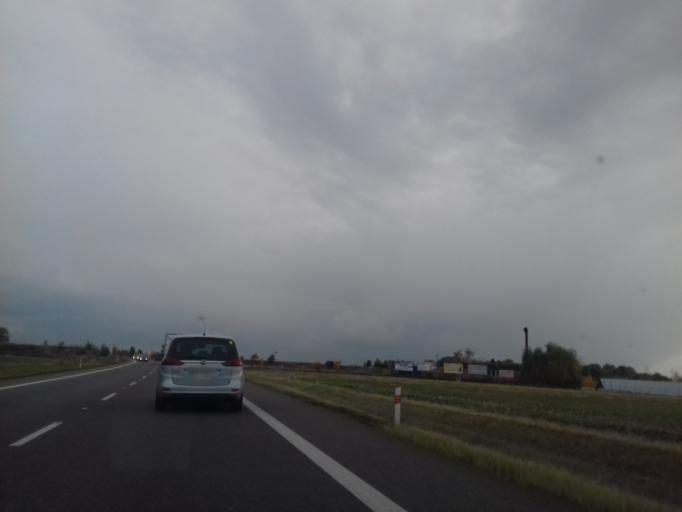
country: CZ
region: Pardubicky
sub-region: Okres Chrudim
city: Chrudim
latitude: 49.9916
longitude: 15.7678
